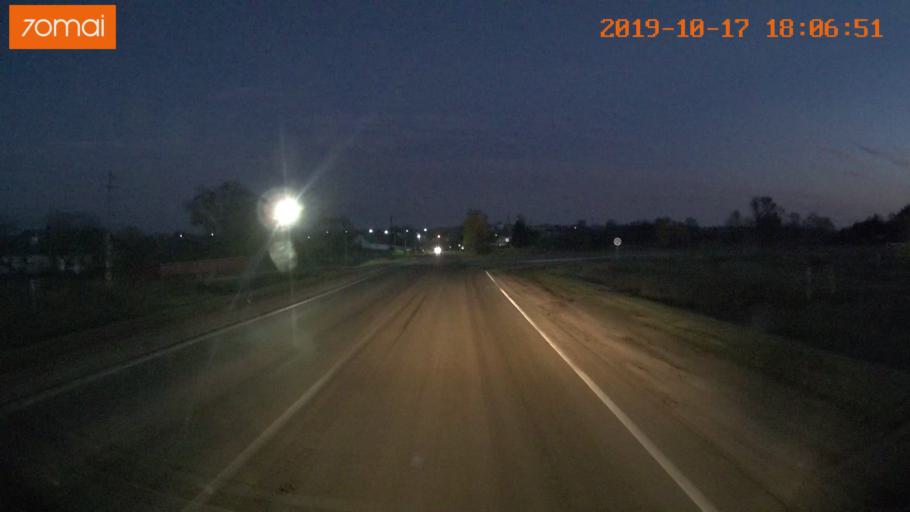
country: RU
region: Tula
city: Kurkino
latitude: 53.4484
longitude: 38.6590
